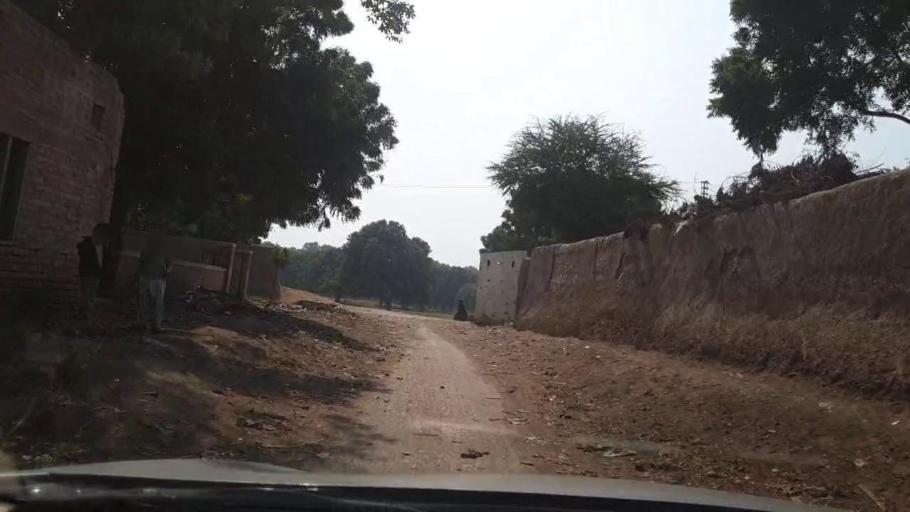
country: PK
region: Sindh
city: Tando Allahyar
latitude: 25.4832
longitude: 68.7712
